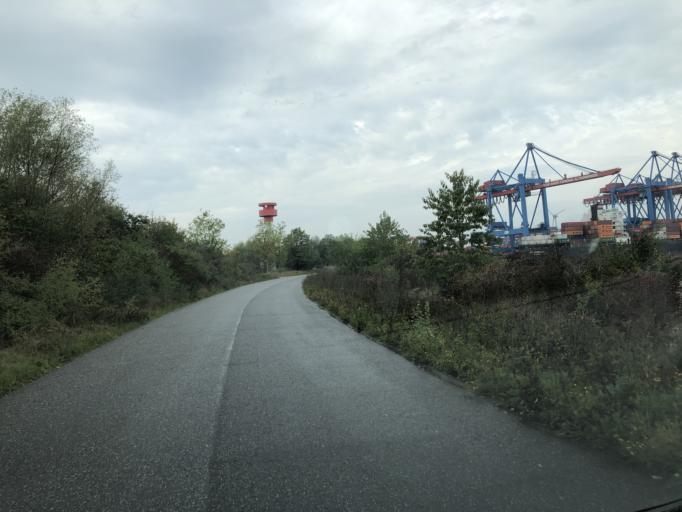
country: DE
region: Hamburg
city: Harburg
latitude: 53.4960
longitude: 9.9424
